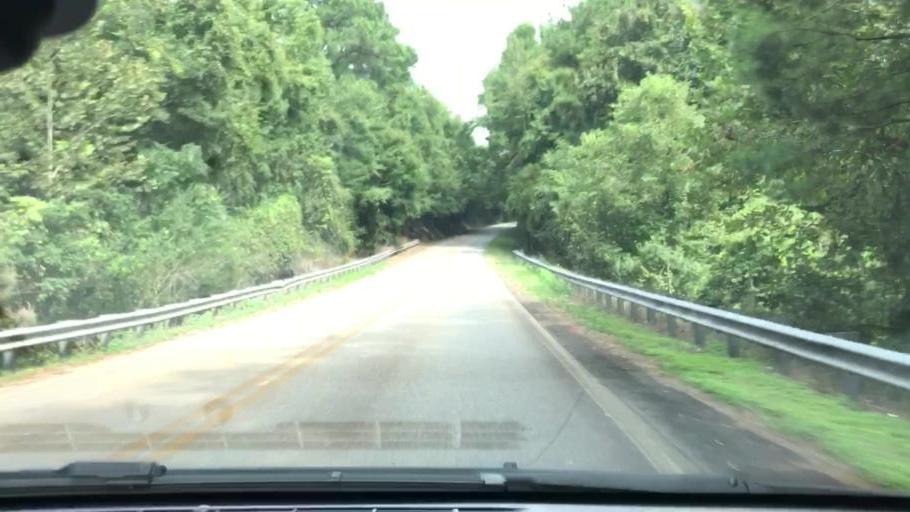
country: US
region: Georgia
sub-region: Clay County
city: Fort Gaines
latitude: 31.5716
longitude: -85.0047
